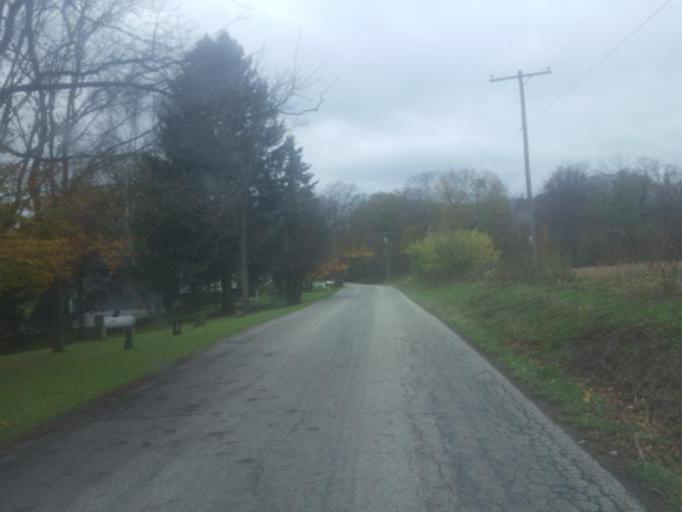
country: US
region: Ohio
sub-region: Richland County
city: Lincoln Heights
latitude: 40.7365
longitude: -82.4671
